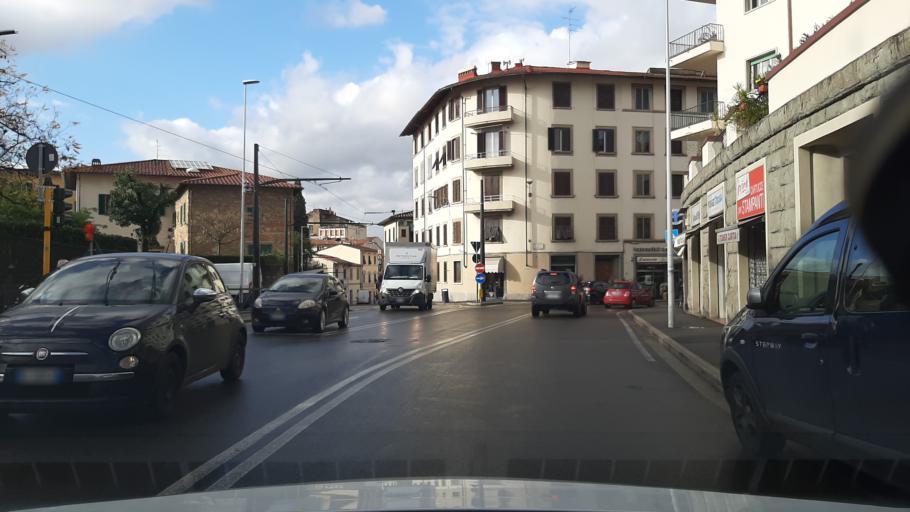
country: IT
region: Tuscany
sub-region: Province of Florence
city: Florence
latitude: 43.7937
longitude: 11.2457
